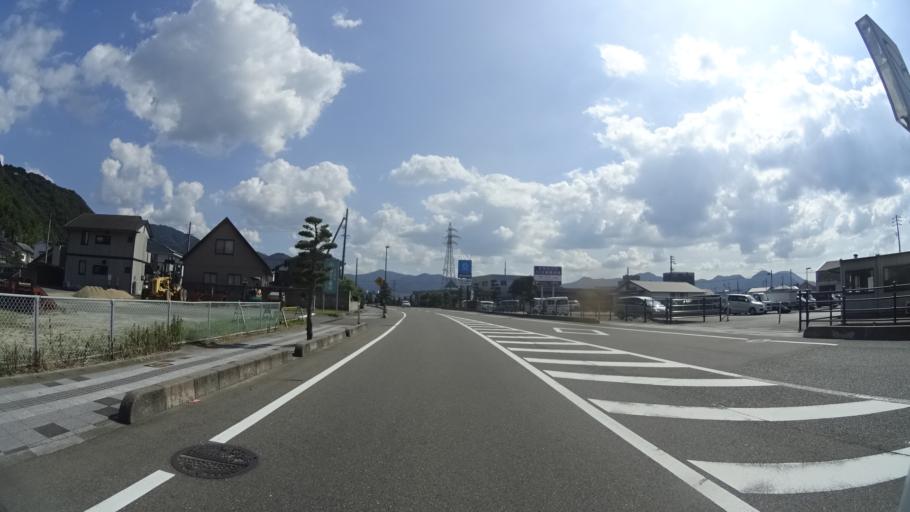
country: JP
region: Yamaguchi
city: Hagi
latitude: 34.4209
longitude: 131.4126
